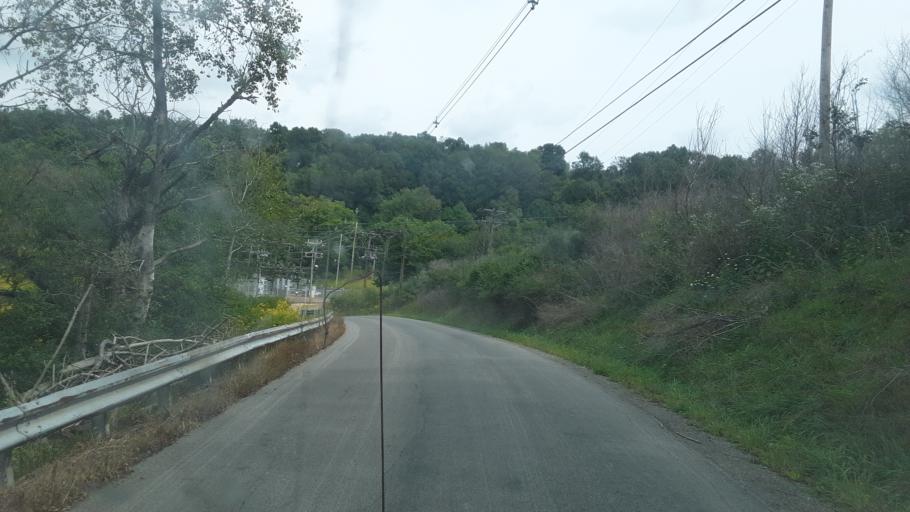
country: US
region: Pennsylvania
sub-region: Jefferson County
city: Punxsutawney
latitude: 40.9471
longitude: -79.1275
